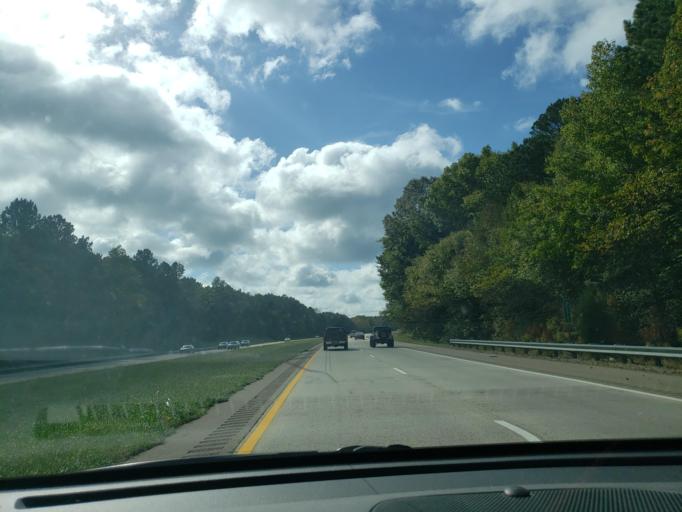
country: US
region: North Carolina
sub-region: Vance County
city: South Henderson
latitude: 36.3208
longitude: -78.4639
